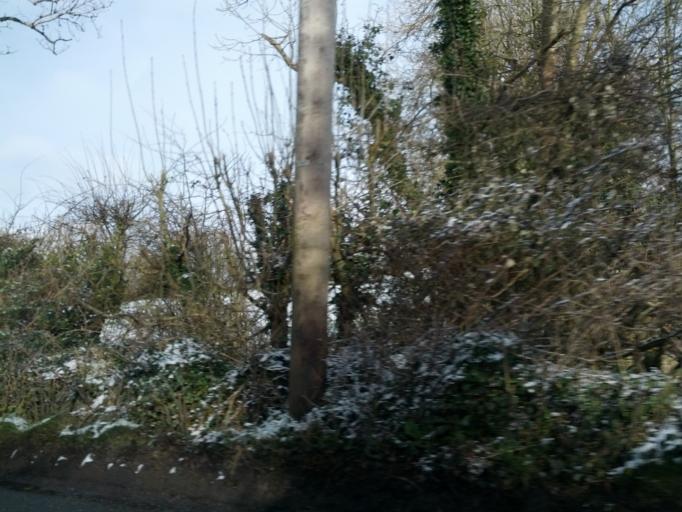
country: IE
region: Connaught
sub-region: County Galway
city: Gort
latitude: 53.1713
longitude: -8.7867
